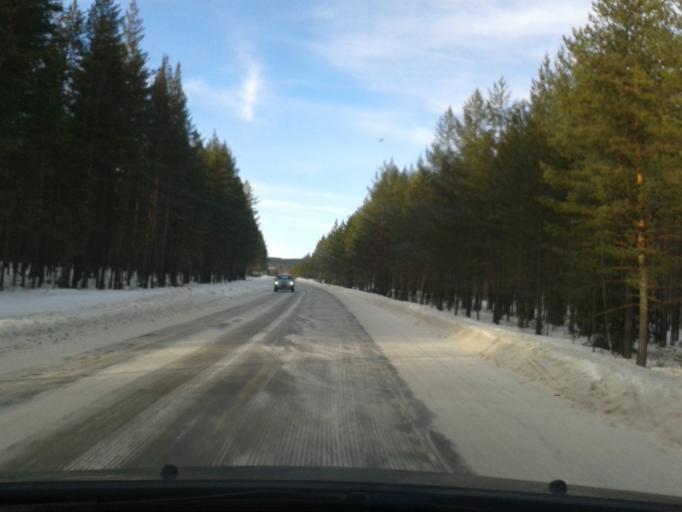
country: SE
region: Vaesternorrland
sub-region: OErnskoeldsviks Kommun
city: Bredbyn
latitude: 63.5590
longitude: 17.9417
